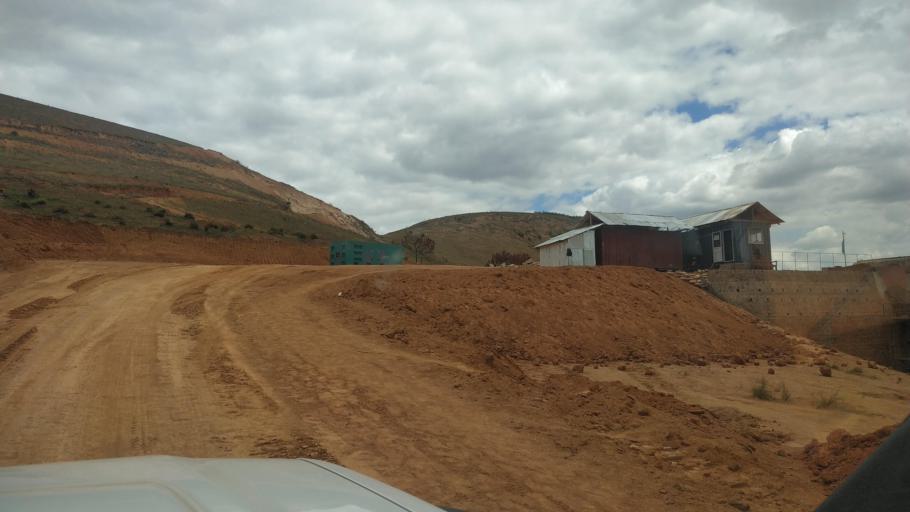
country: MG
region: Alaotra Mangoro
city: Ambatondrazaka
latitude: -17.8835
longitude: 48.2929
